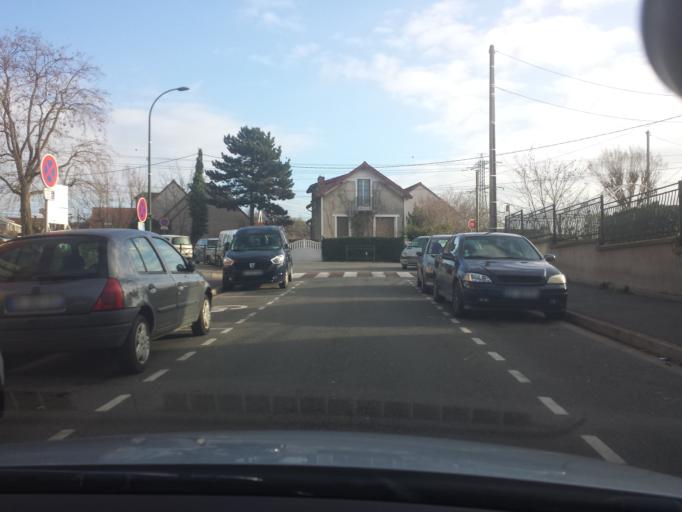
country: FR
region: Ile-de-France
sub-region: Departement de l'Essonne
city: Palaiseau
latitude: 48.7152
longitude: 2.2624
